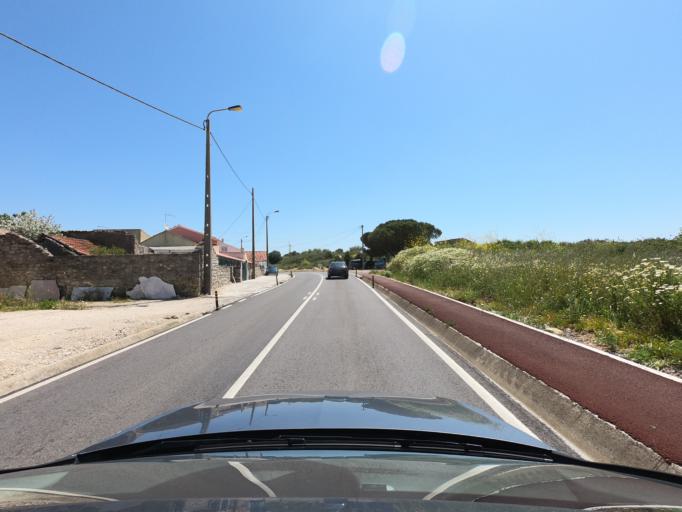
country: PT
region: Lisbon
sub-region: Cascais
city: Sao Domingos de Rana
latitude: 38.7329
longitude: -9.3494
